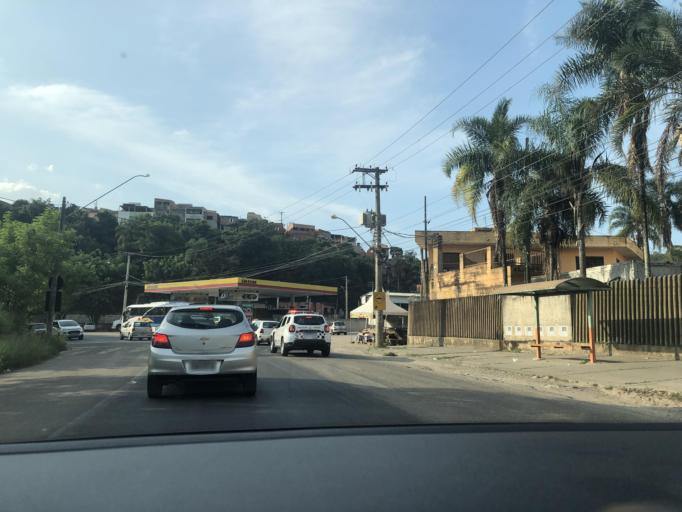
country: BR
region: Sao Paulo
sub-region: Aruja
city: Aruja
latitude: -23.3221
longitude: -46.4258
